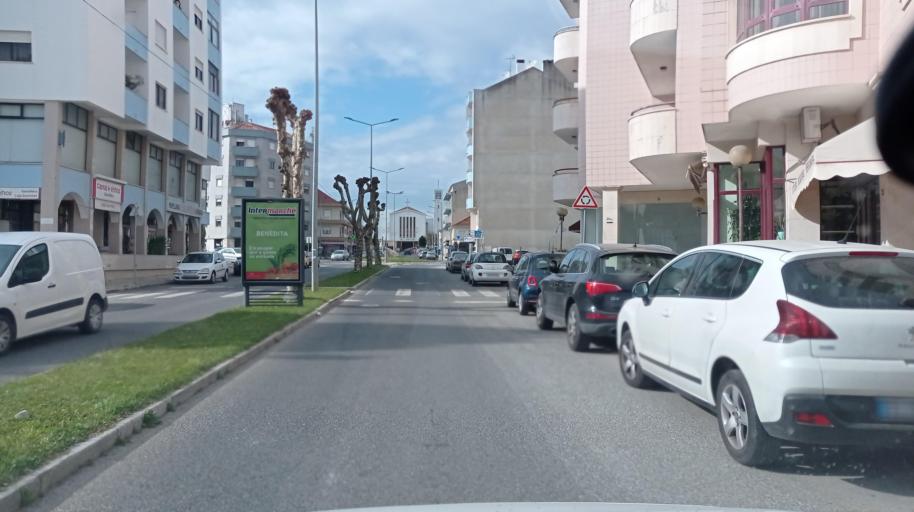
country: PT
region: Leiria
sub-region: Alcobaca
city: Benedita
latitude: 39.4256
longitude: -8.9790
